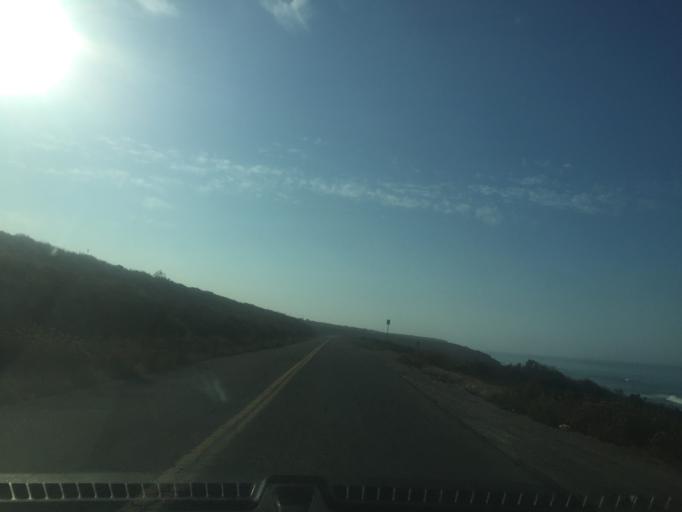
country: US
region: California
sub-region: Santa Barbara County
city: Lompoc
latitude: 34.5057
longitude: -120.4992
